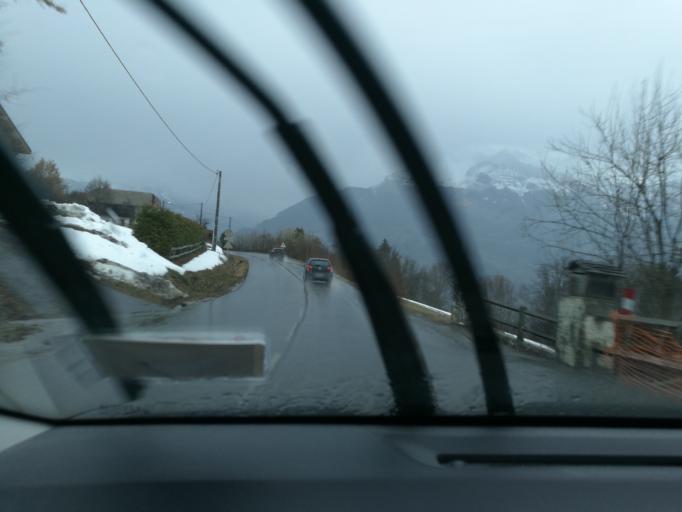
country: FR
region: Rhone-Alpes
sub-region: Departement de la Haute-Savoie
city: Saint-Gervais-les-Bains
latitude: 45.8923
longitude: 6.7012
